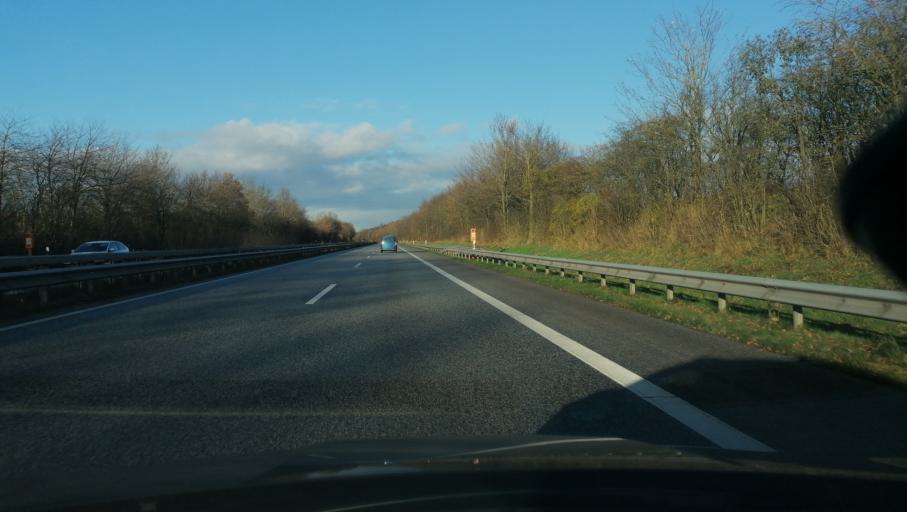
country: DE
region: Schleswig-Holstein
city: Ottenbuttel
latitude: 53.9753
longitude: 9.4921
